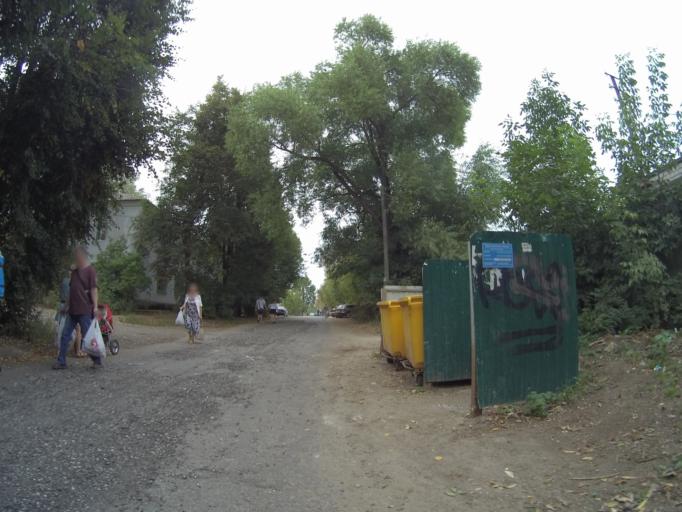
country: RU
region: Vladimir
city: Vladimir
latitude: 56.1219
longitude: 40.3594
